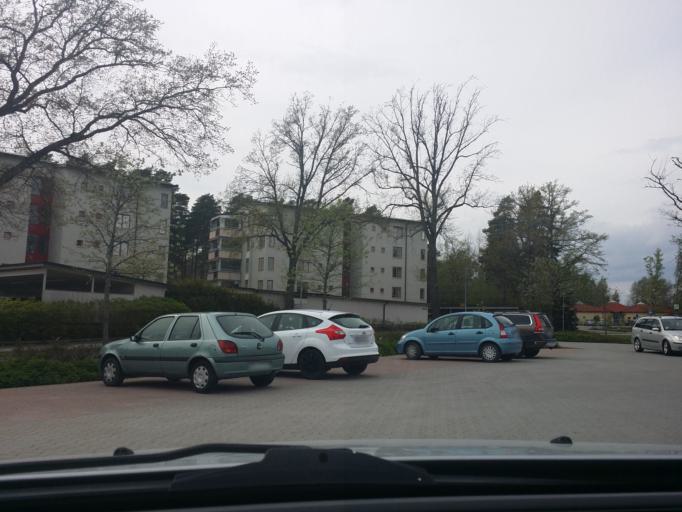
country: SE
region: Vaestmanland
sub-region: Vasteras
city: Vasteras
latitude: 59.6008
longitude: 16.5901
